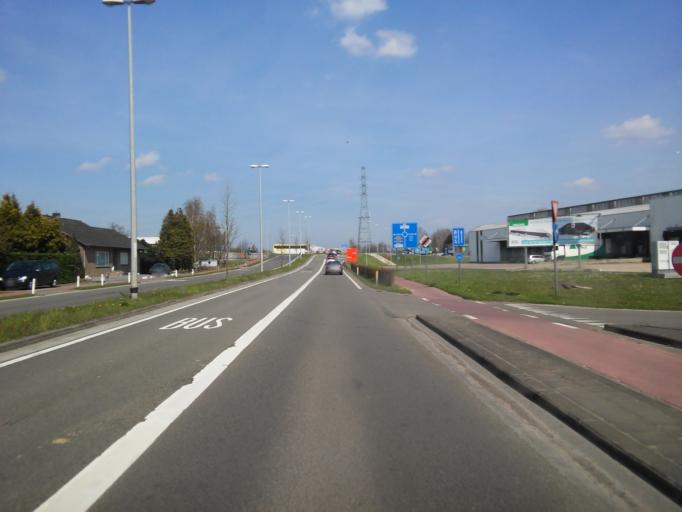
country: BE
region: Flanders
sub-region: Provincie Vlaams-Brabant
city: Boortmeerbeek
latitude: 50.9539
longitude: 4.5916
